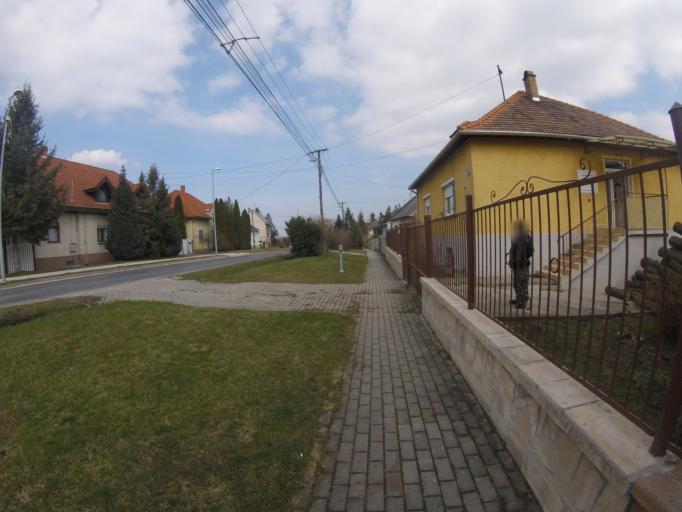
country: HU
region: Komarom-Esztergom
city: Nyergesujfalu
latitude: 47.7570
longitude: 18.5557
